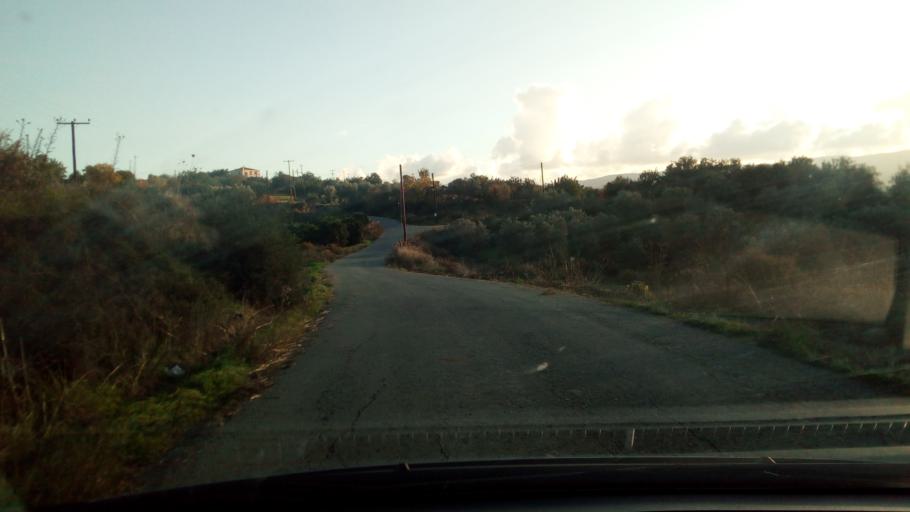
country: CY
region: Pafos
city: Polis
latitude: 34.9878
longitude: 32.4748
